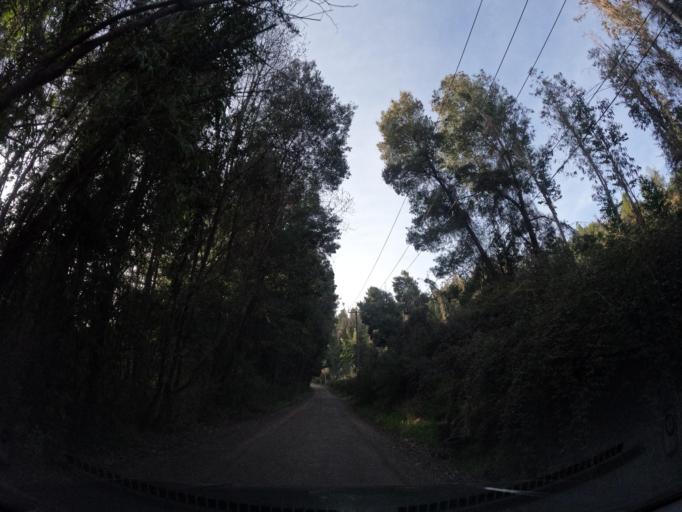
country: CL
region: Biobio
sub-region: Provincia de Concepcion
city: Chiguayante
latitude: -36.8697
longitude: -72.9953
